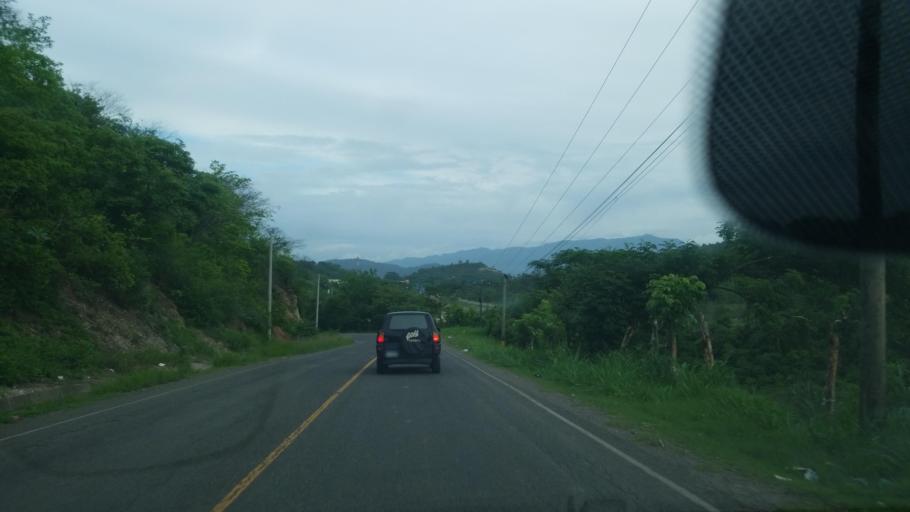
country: HN
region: Santa Barbara
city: Santa Barbara
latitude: 14.9146
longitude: -88.2530
